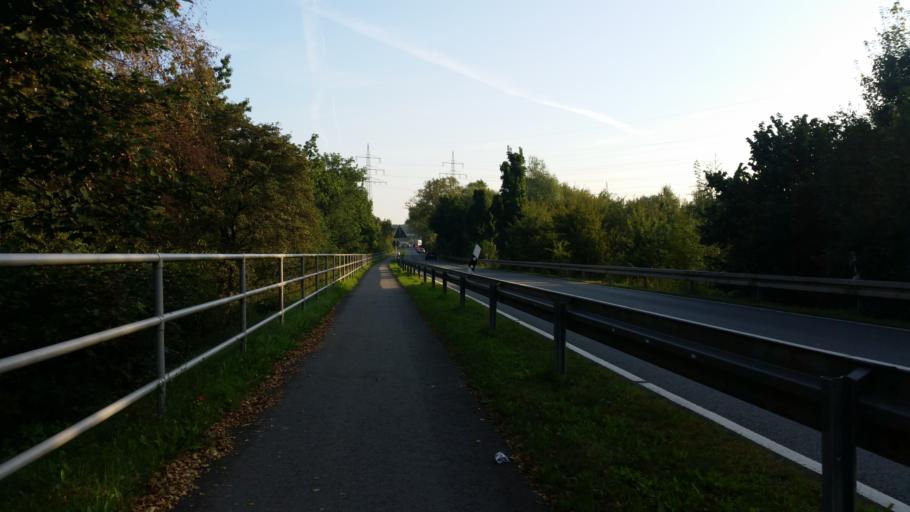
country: DE
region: Lower Saxony
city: Weyhausen
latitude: 52.4267
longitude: 10.7329
